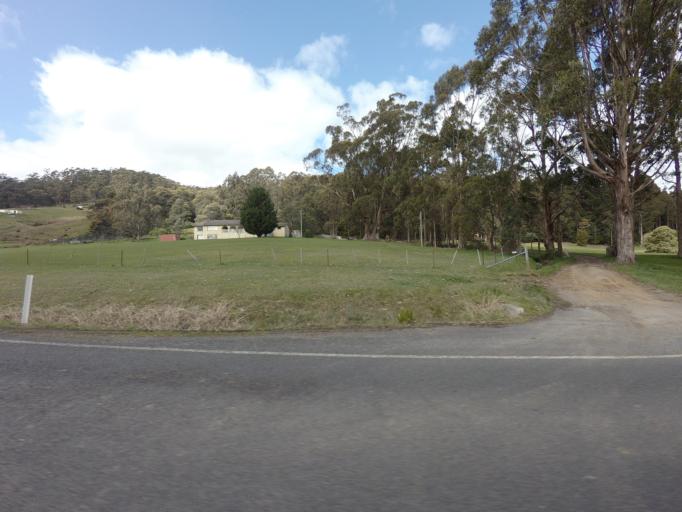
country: AU
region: Tasmania
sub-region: Huon Valley
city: Cygnet
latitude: -43.2971
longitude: 147.0106
